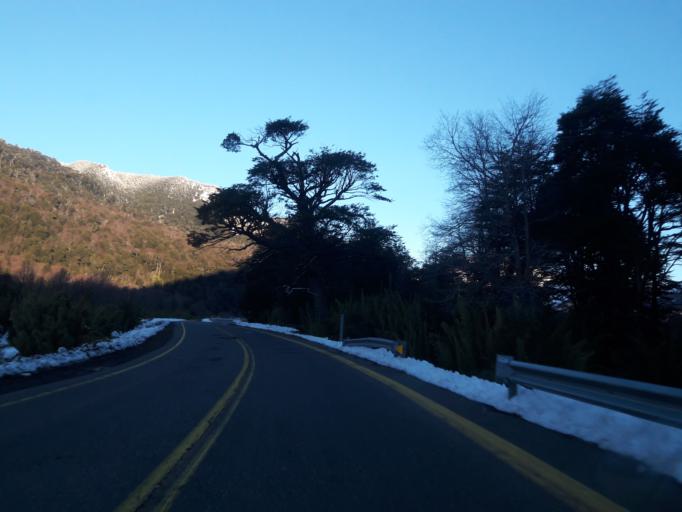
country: CL
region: Araucania
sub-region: Provincia de Cautin
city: Vilcun
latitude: -38.4908
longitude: -71.5249
